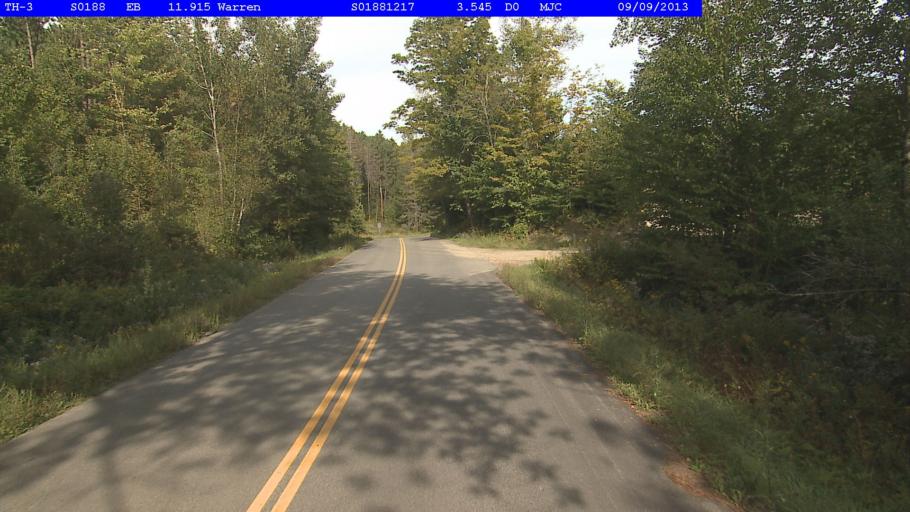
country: US
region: Vermont
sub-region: Washington County
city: Northfield
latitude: 44.1062
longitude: -72.8630
